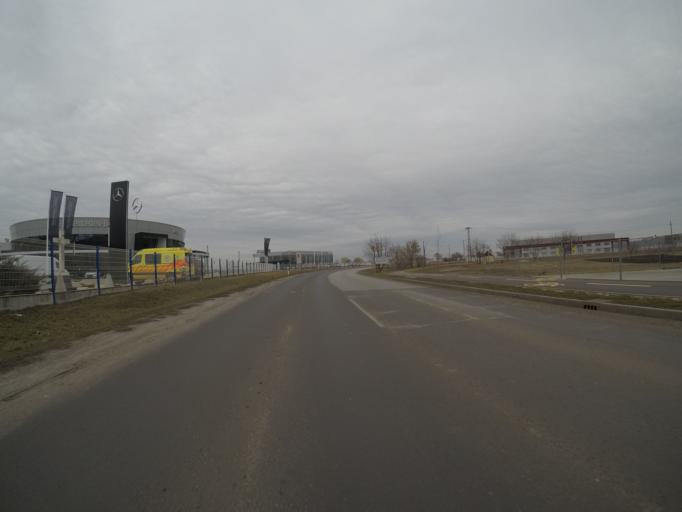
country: HU
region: Jasz-Nagykun-Szolnok
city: Jaszbereny
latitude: 47.5060
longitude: 19.9301
